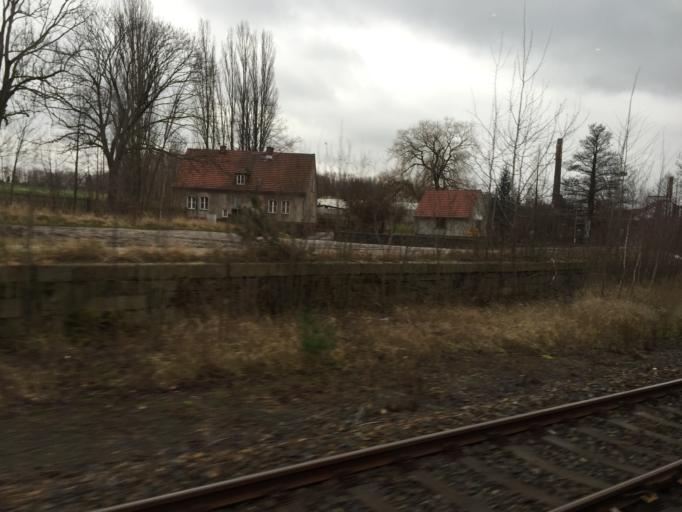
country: DE
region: Saxony
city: Reichenbach
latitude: 51.1351
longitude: 14.7987
